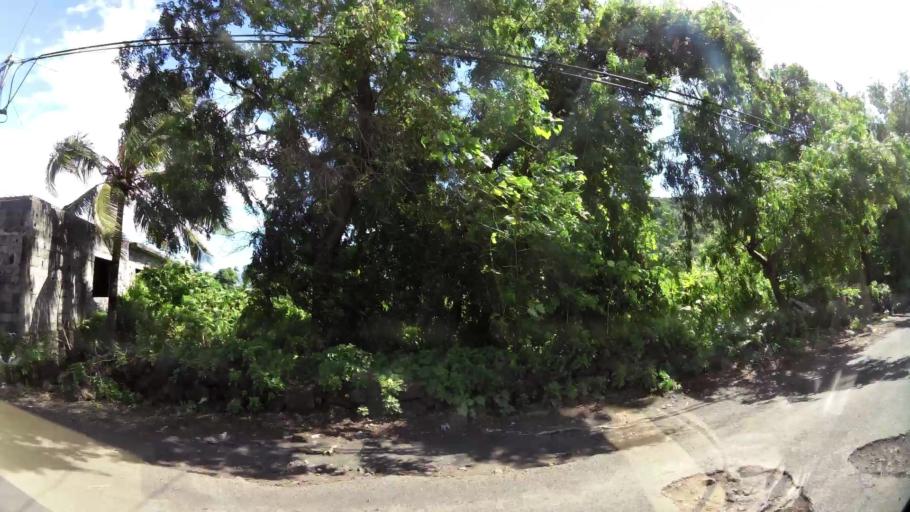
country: KM
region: Grande Comore
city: Mavingouni
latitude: -11.7435
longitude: 43.2386
